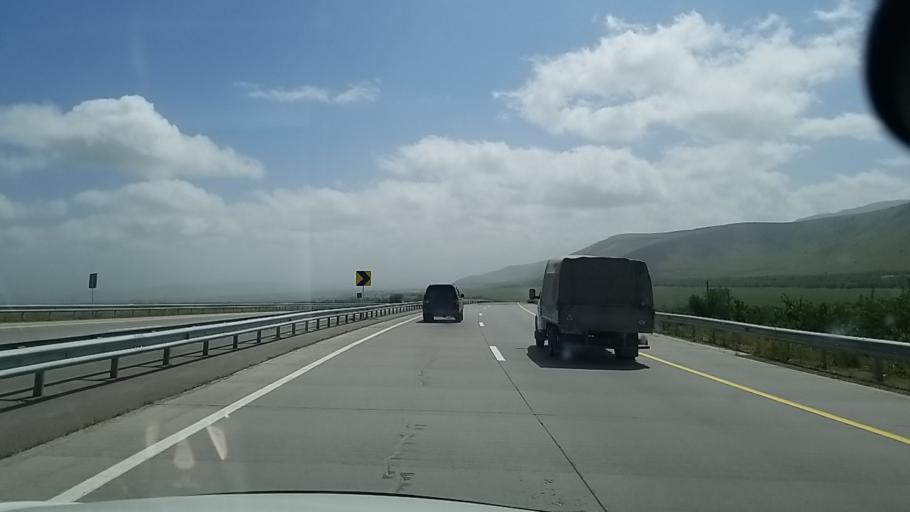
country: KZ
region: Ongtustik Qazaqstan
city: Sastobe
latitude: 42.5413
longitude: 70.0318
